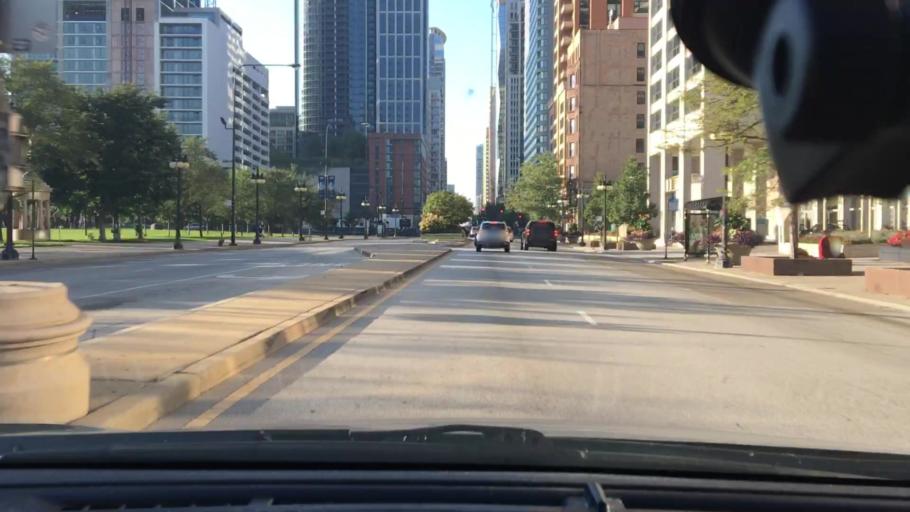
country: US
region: Illinois
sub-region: Cook County
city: Chicago
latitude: 41.8692
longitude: -87.6242
